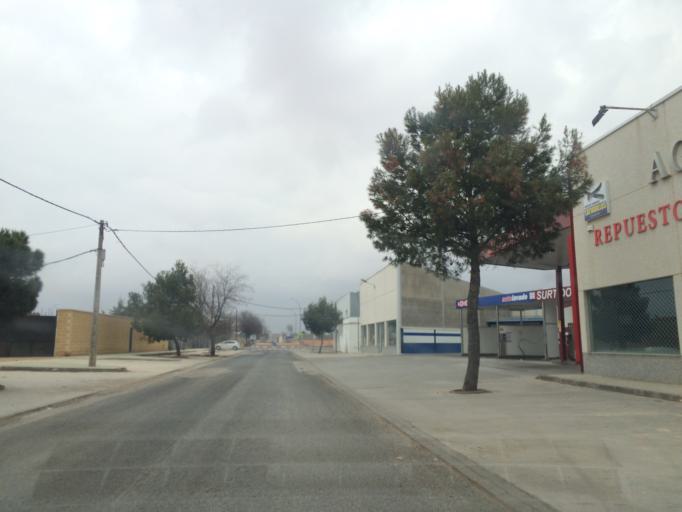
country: ES
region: Castille-La Mancha
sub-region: Province of Toledo
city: Madridejos
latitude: 39.4751
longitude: -3.5282
